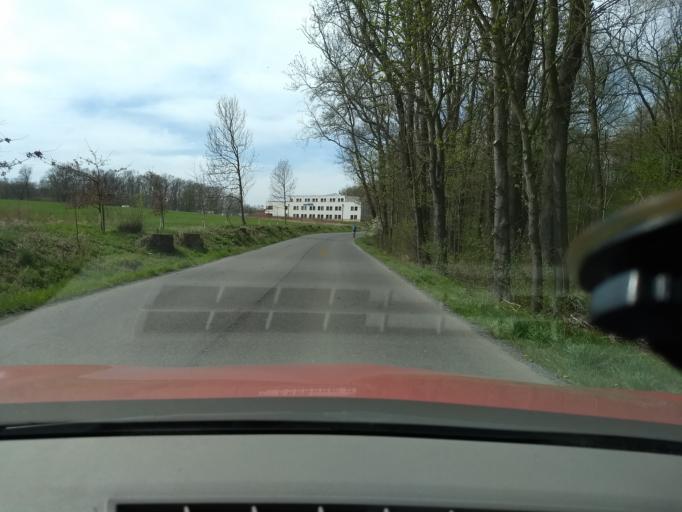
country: CZ
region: Central Bohemia
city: Hostivice
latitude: 50.0685
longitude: 14.2520
